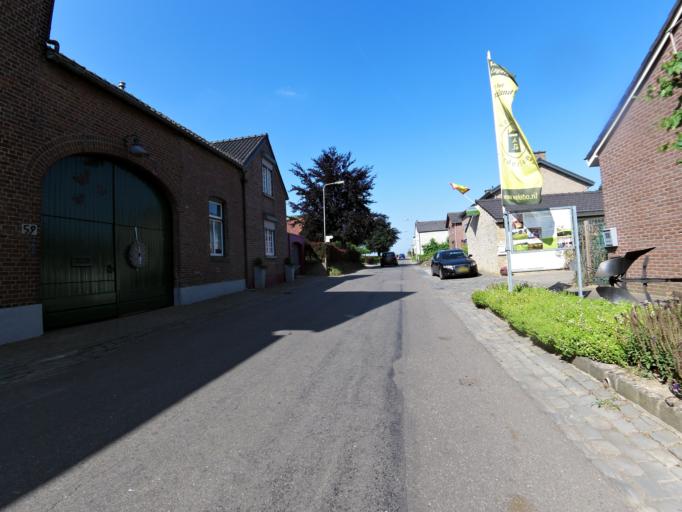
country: NL
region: Limburg
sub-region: Valkenburg aan de Geul
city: Schin op Geul
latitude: 50.8684
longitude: 5.8677
